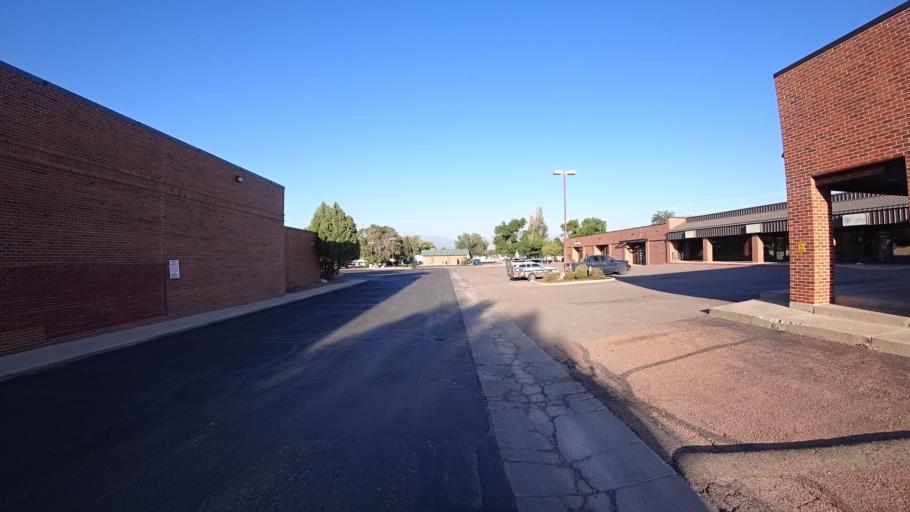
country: US
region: Colorado
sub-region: El Paso County
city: Cimarron Hills
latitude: 38.8886
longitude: -104.7550
